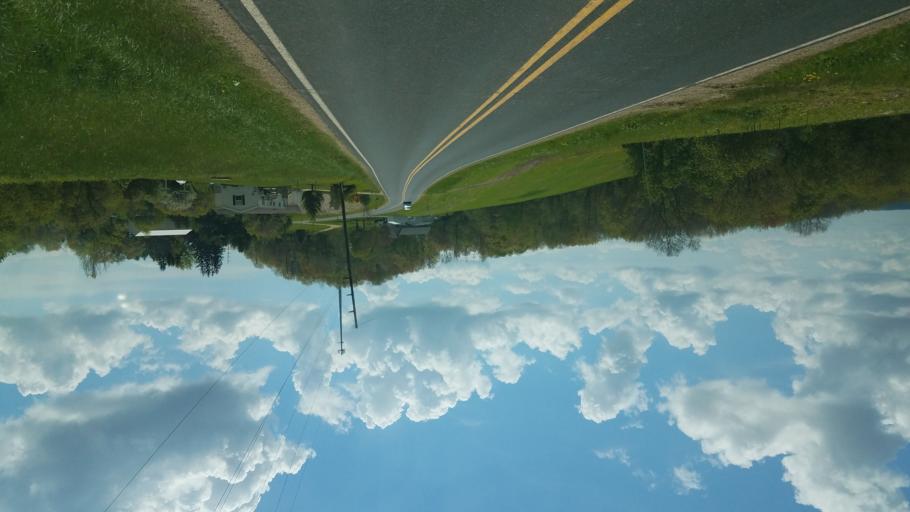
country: US
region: Wisconsin
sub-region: Vernon County
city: Hillsboro
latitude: 43.6655
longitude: -90.3486
